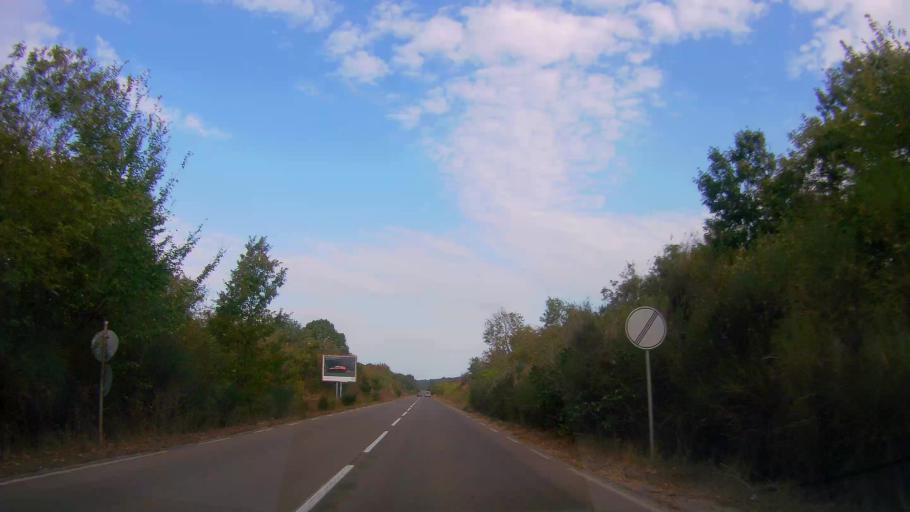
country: BG
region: Burgas
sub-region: Obshtina Sozopol
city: Sozopol
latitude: 42.3487
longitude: 27.7127
